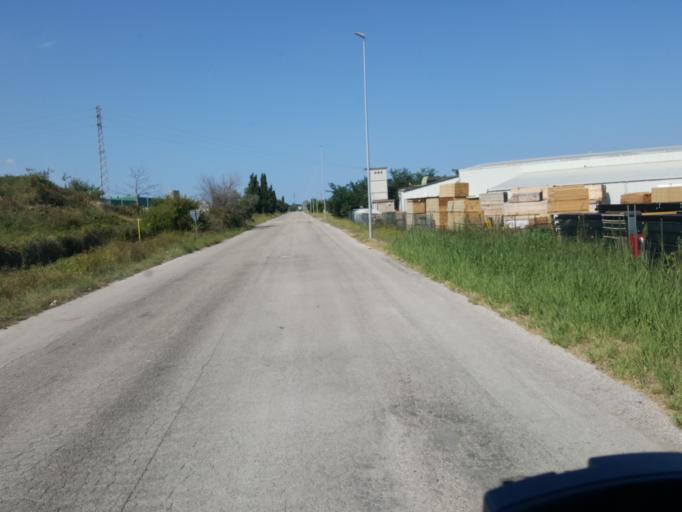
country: IT
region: Abruzzo
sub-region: Provincia di Chieti
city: Salvo Marina
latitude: 42.0607
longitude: 14.7632
